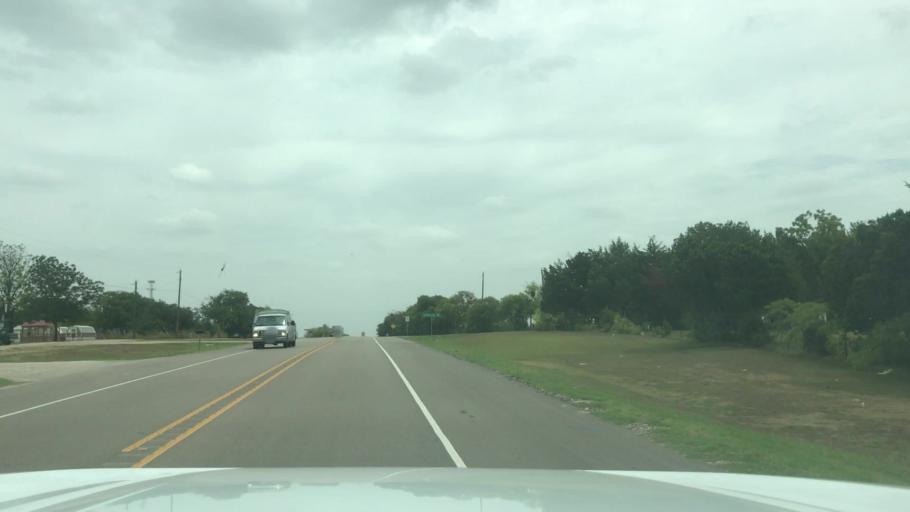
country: US
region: Texas
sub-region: McLennan County
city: Woodway
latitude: 31.5855
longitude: -97.3162
